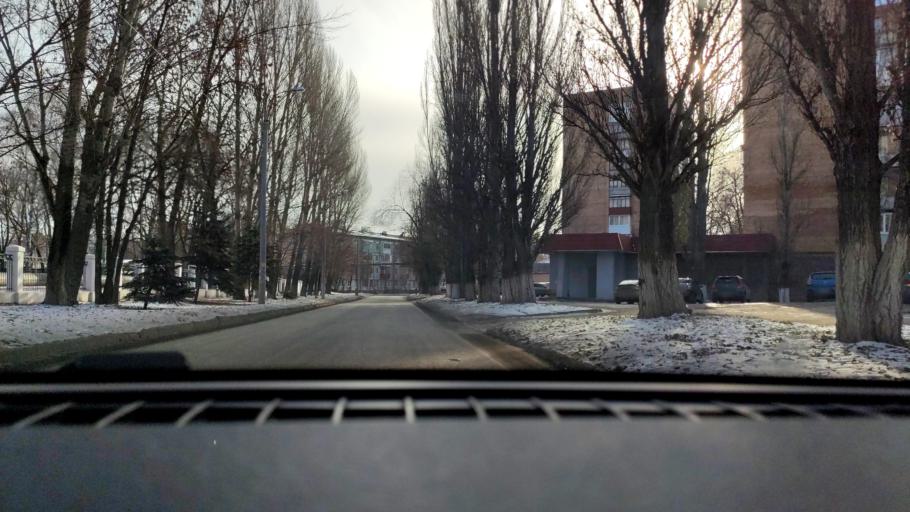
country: RU
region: Samara
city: Petra-Dubrava
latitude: 53.3004
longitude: 50.2805
